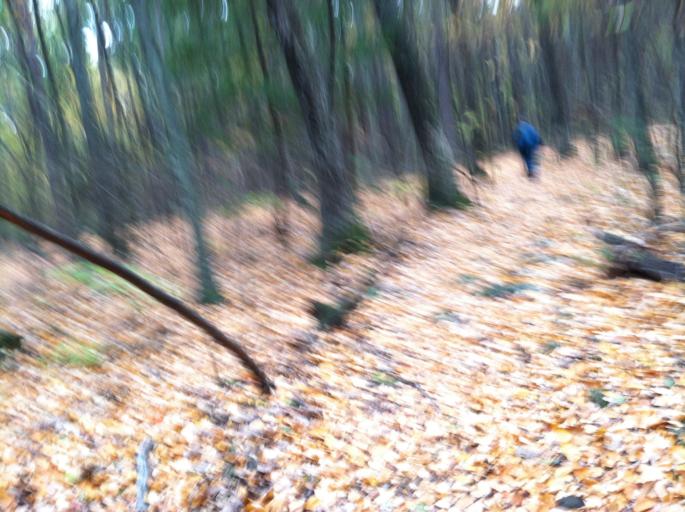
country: US
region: Massachusetts
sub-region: Middlesex County
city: Carlisle
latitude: 42.4956
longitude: -71.3598
